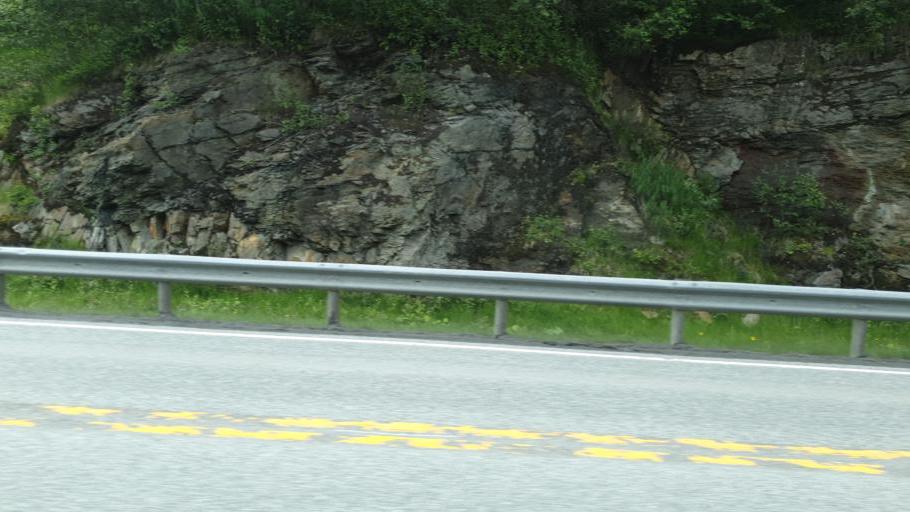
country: NO
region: Sor-Trondelag
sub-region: Midtre Gauldal
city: Storen
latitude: 62.9284
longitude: 10.1672
